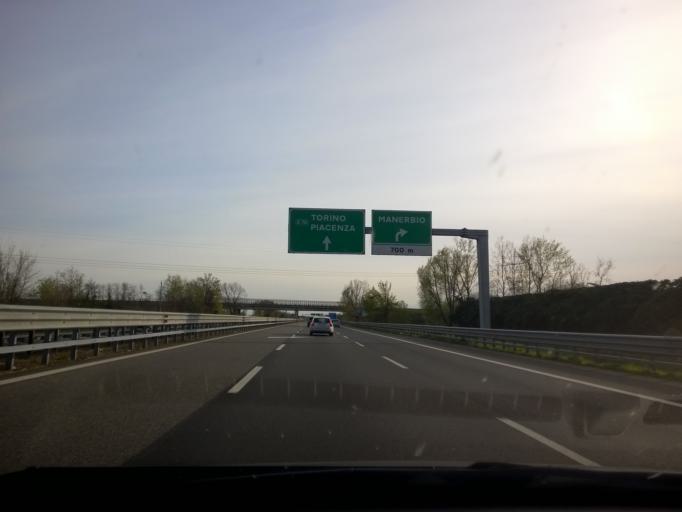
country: IT
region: Lombardy
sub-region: Provincia di Brescia
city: Manerbio
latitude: 45.3740
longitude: 10.1740
